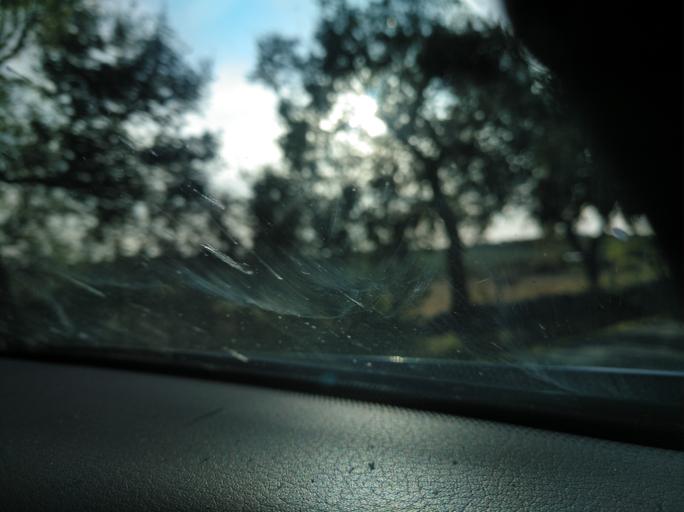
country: PT
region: Evora
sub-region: Estremoz
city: Estremoz
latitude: 38.9490
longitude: -7.4931
